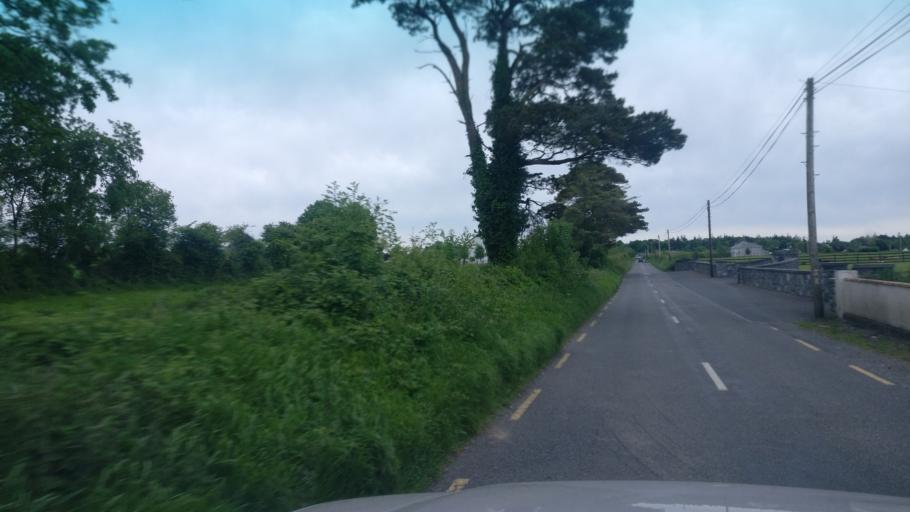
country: IE
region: Connaught
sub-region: County Galway
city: Portumna
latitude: 53.0956
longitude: -8.2417
